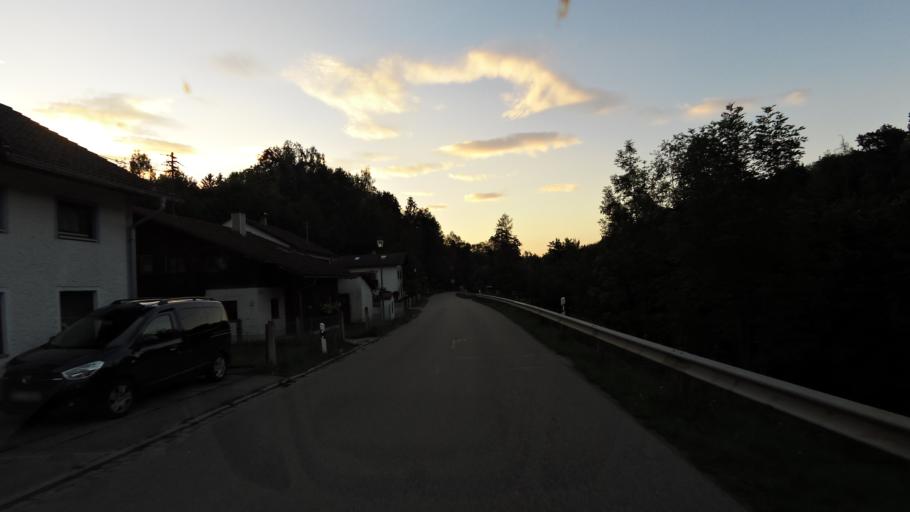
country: DE
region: Bavaria
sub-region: Upper Bavaria
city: Kraiburg am Inn
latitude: 48.1700
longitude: 12.4282
